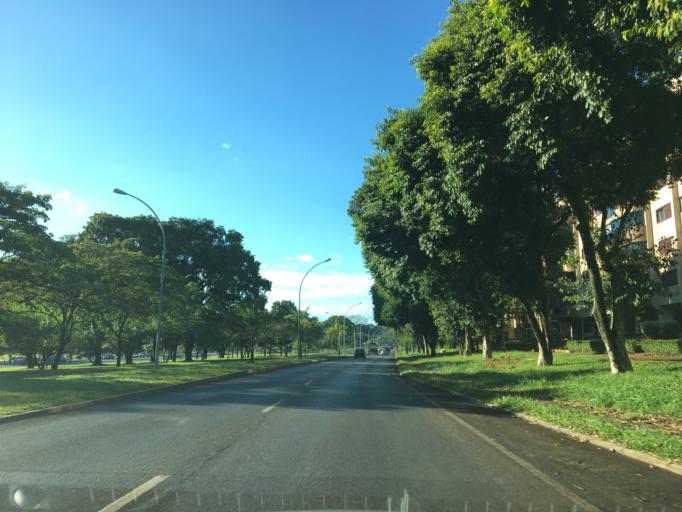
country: BR
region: Federal District
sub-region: Brasilia
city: Brasilia
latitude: -15.7495
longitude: -47.8889
